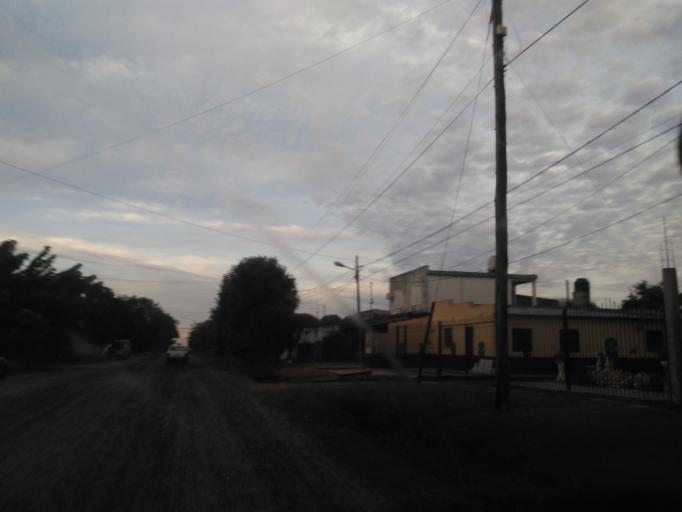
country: AR
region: Chaco
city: Resistencia
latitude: -27.4737
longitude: -58.9973
